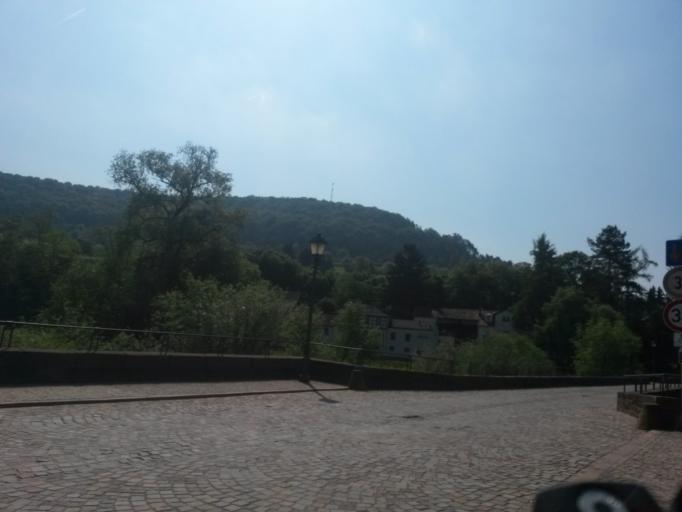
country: DE
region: Bavaria
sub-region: Regierungsbezirk Unterfranken
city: Euerdorf
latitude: 50.1516
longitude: 10.0269
